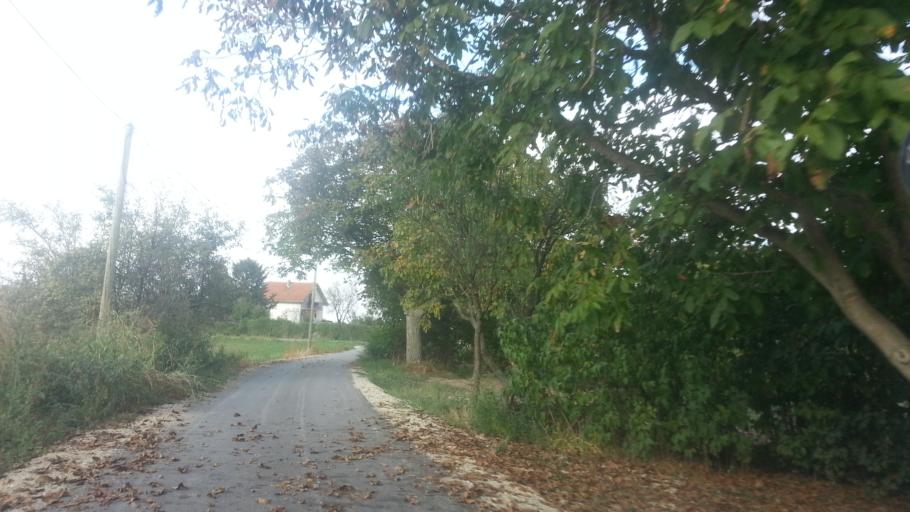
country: RS
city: Belegis
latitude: 45.0226
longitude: 20.3491
